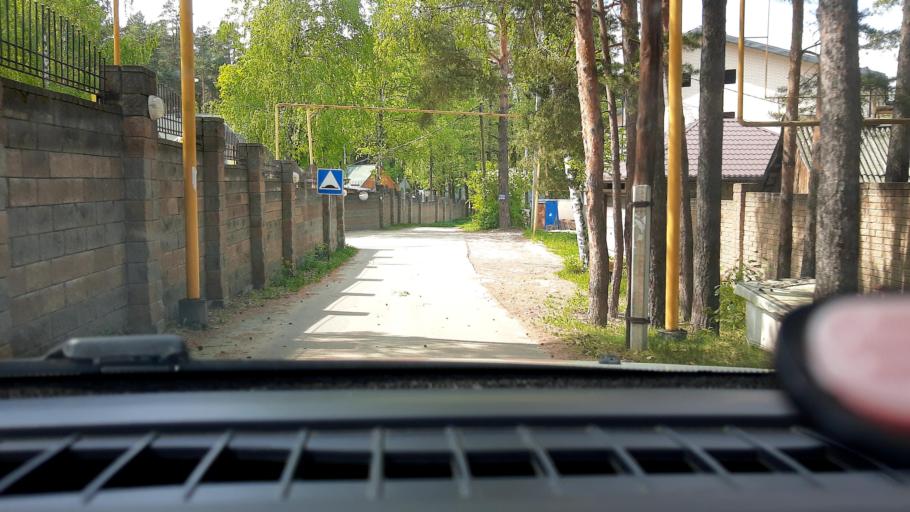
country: RU
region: Nizjnij Novgorod
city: Afonino
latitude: 56.1850
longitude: 44.1022
